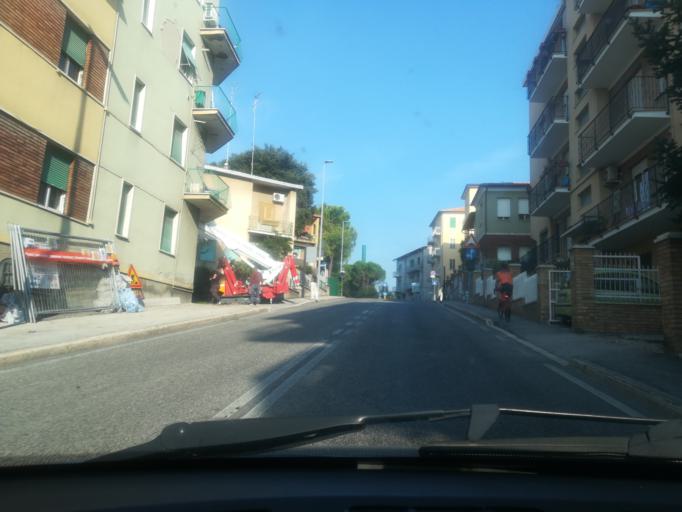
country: IT
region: The Marches
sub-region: Provincia di Macerata
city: Macerata
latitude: 43.2922
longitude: 13.4600
